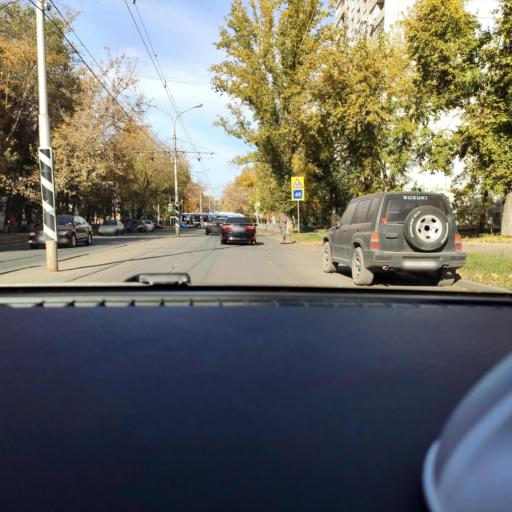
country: RU
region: Samara
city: Samara
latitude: 53.1987
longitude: 50.1391
